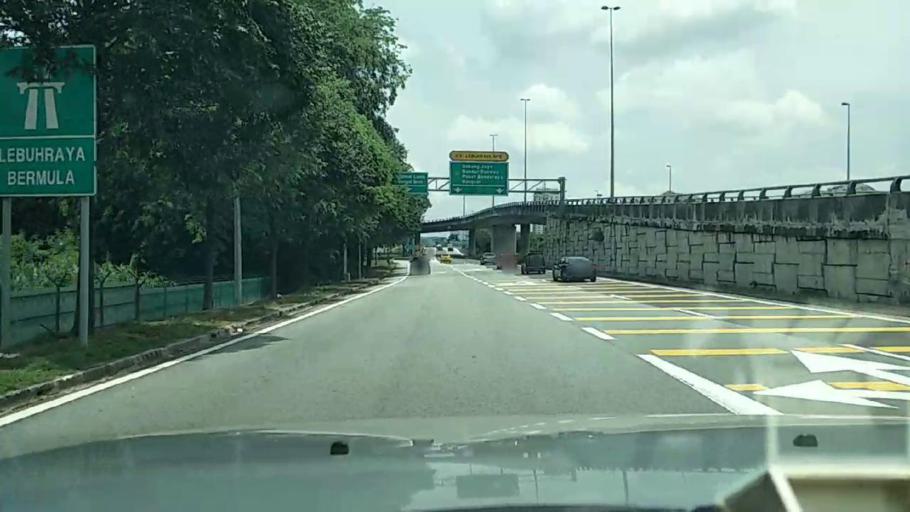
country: MY
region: Kuala Lumpur
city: Kuala Lumpur
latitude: 3.0945
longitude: 101.6915
